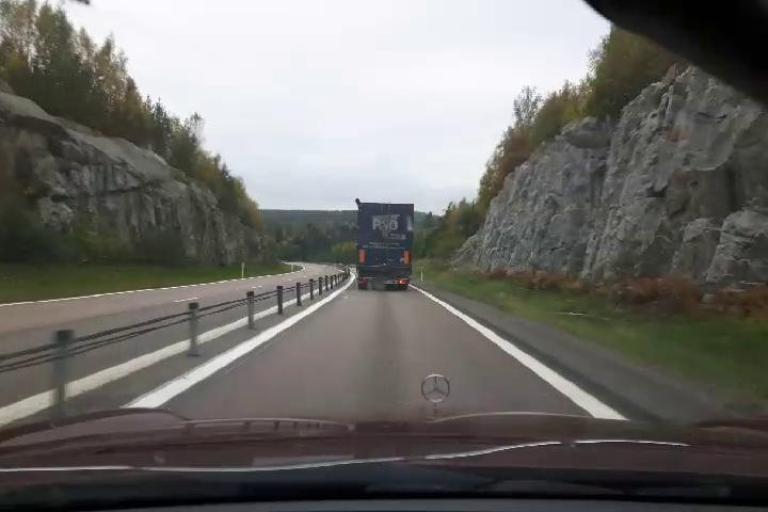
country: SE
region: Vaesternorrland
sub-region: Haernoesands Kommun
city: Haernoesand
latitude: 62.8353
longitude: 17.9680
